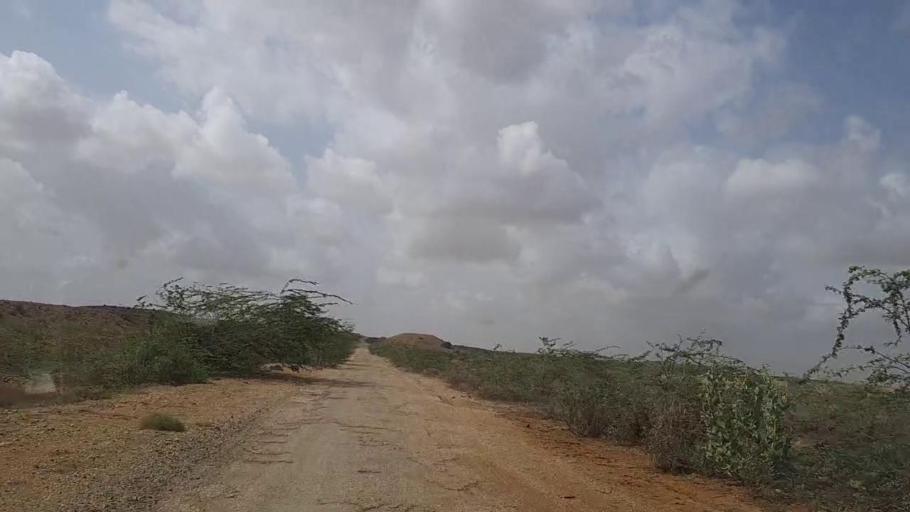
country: PK
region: Sindh
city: Thatta
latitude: 24.8838
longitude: 67.8963
